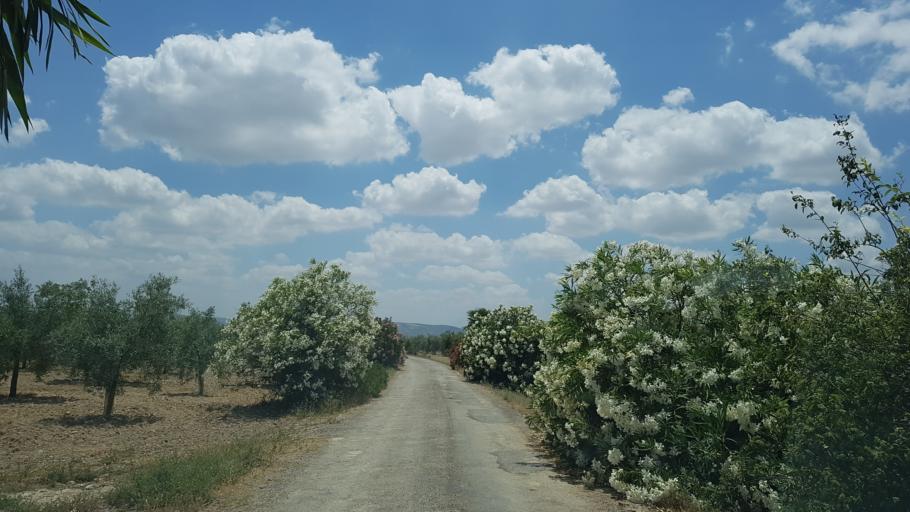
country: ES
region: Andalusia
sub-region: Province of Cordoba
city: Cabra
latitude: 37.5263
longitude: -4.4588
